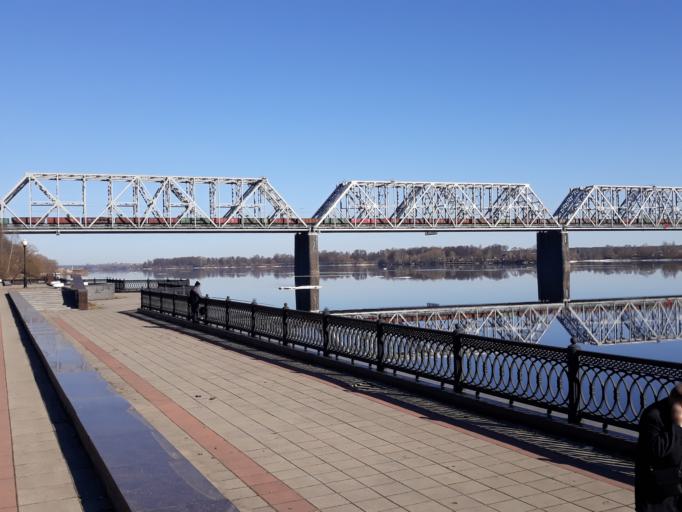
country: RU
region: Jaroslavl
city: Yaroslavl
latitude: 57.6434
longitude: 39.8853
